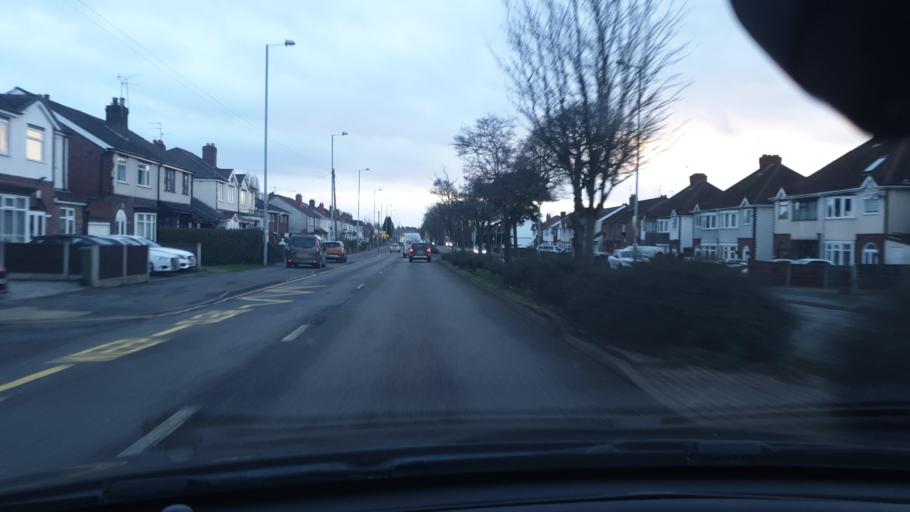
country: GB
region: England
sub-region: Staffordshire
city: Featherstone
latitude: 52.6258
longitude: -2.1275
